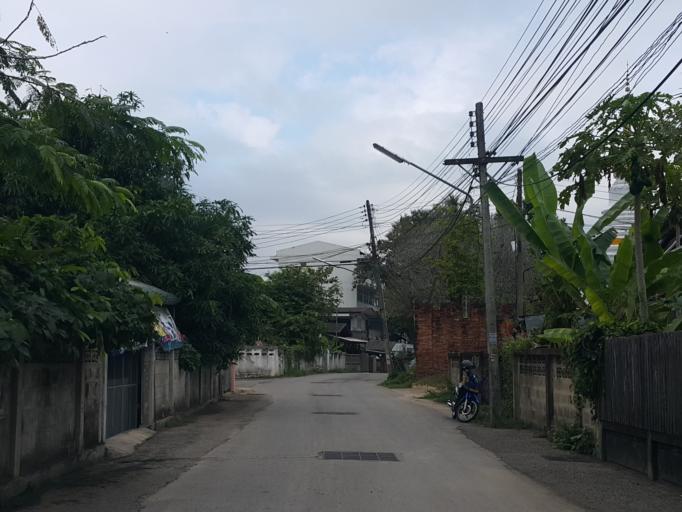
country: TH
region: Lampang
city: Lampang
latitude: 18.2999
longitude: 99.5095
